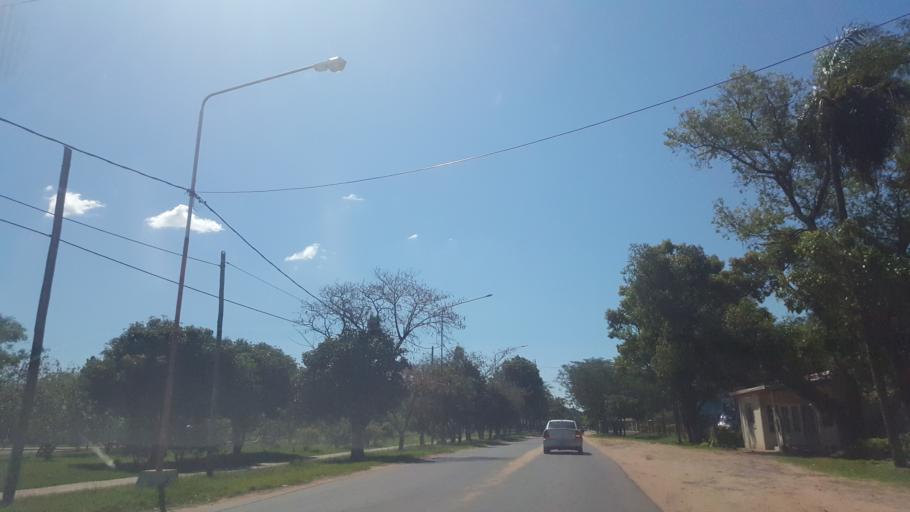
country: AR
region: Corrientes
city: Ituzaingo
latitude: -27.5925
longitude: -56.6855
